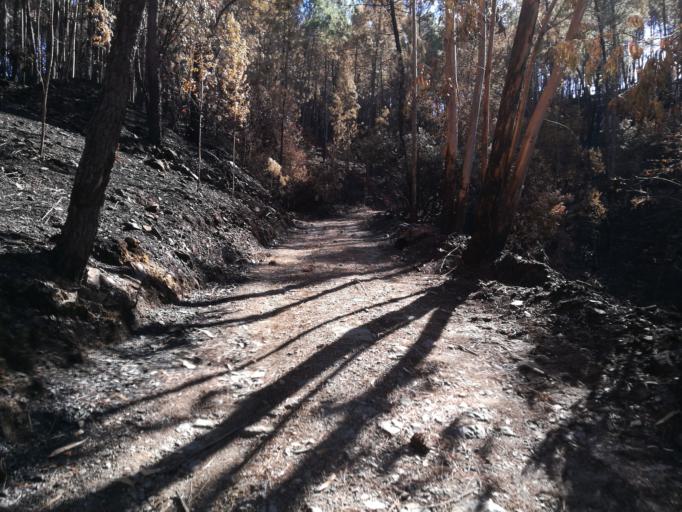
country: PT
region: Leiria
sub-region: Pedrogao Grande
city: Pedrogao Grande
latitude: 39.9145
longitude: -8.0646
